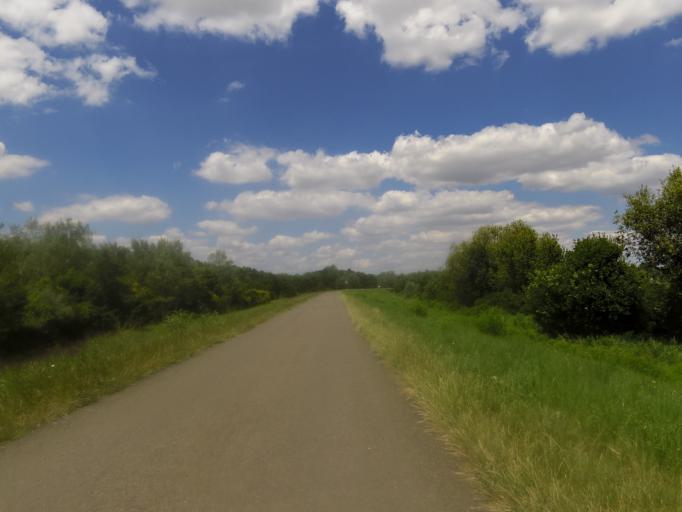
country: HU
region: Heves
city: Tiszanana
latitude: 47.5748
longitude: 20.6105
